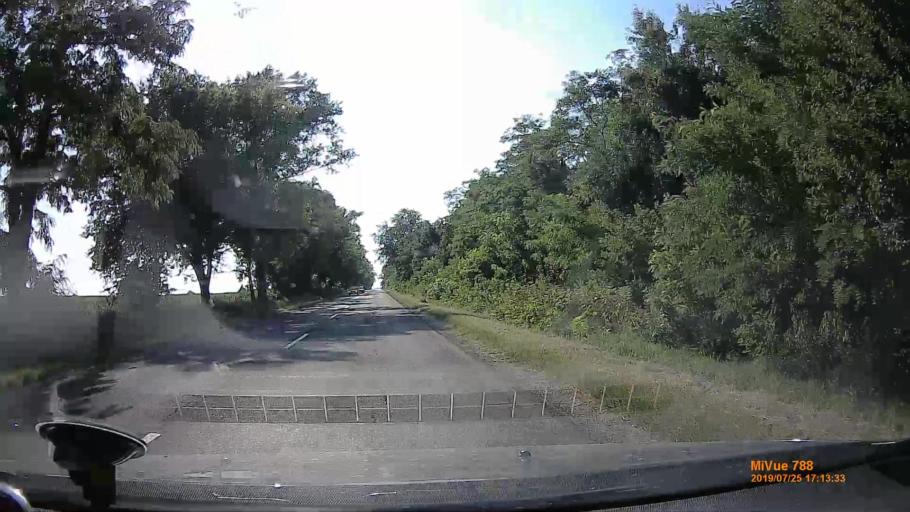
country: HU
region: Pest
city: Hevizgyoerk
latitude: 47.6487
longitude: 19.5145
